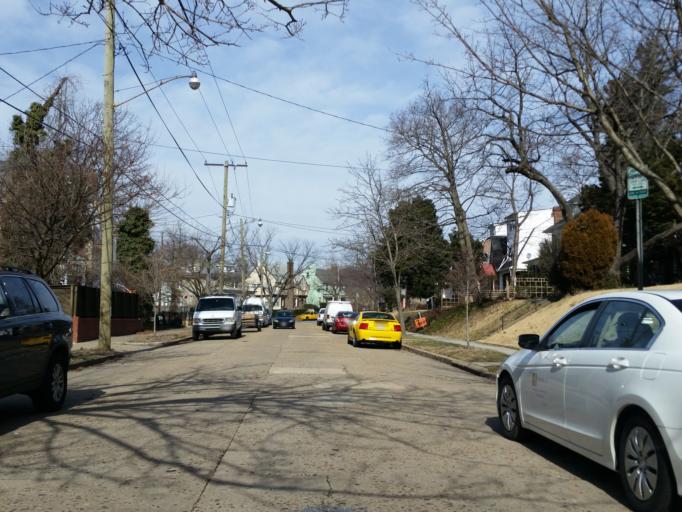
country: US
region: Maryland
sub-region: Montgomery County
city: Silver Spring
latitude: 38.9818
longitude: -77.0279
